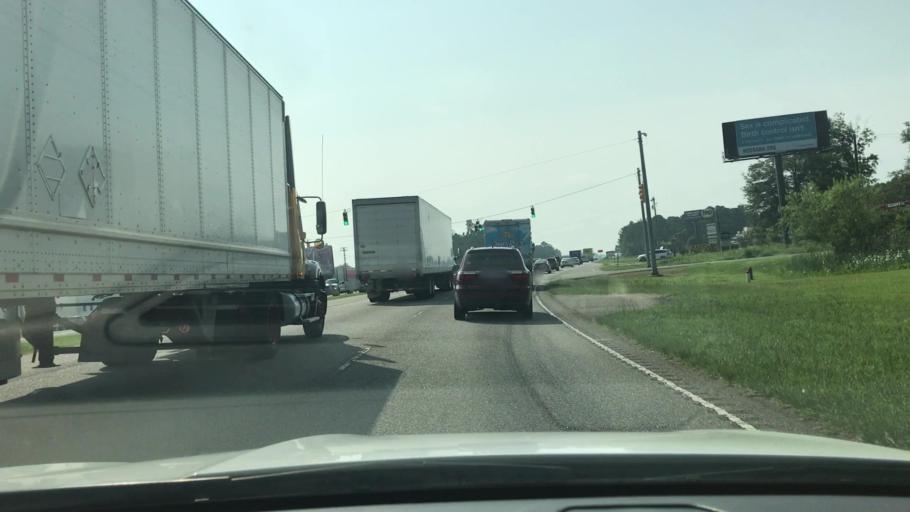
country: US
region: South Carolina
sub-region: Horry County
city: Red Hill
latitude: 33.8057
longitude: -79.0107
